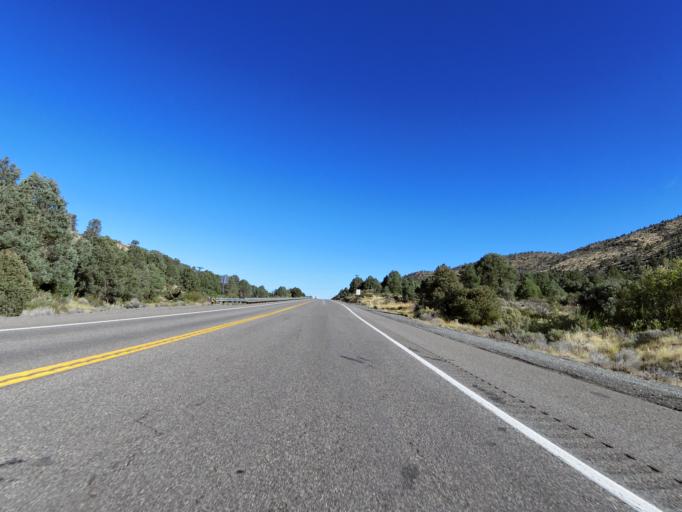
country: US
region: Nevada
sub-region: Douglas County
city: Gardnerville Ranchos
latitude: 38.7608
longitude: -119.5760
